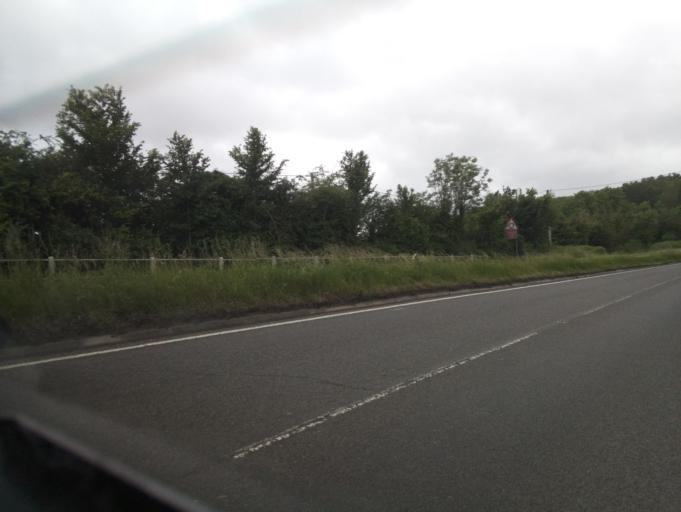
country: GB
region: England
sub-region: Leicestershire
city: Markfield
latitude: 52.6764
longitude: -1.2548
